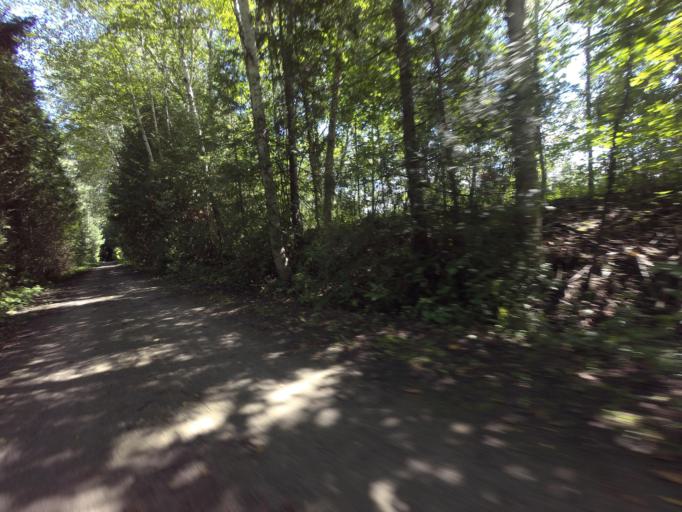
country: CA
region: Ontario
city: Orangeville
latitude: 43.7850
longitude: -80.1527
